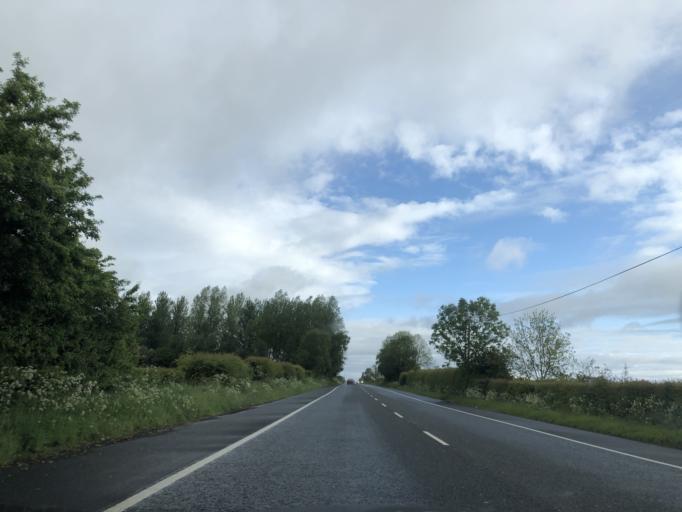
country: GB
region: Northern Ireland
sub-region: Ballymoney District
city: Ballymoney
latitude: 55.1238
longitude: -6.5525
